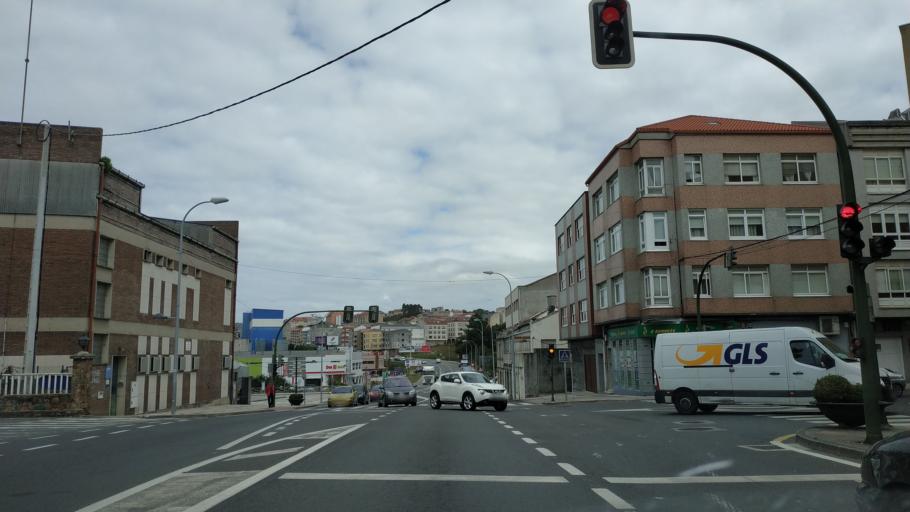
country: ES
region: Galicia
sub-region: Provincia da Coruna
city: Arteixo
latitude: 43.3060
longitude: -8.5081
